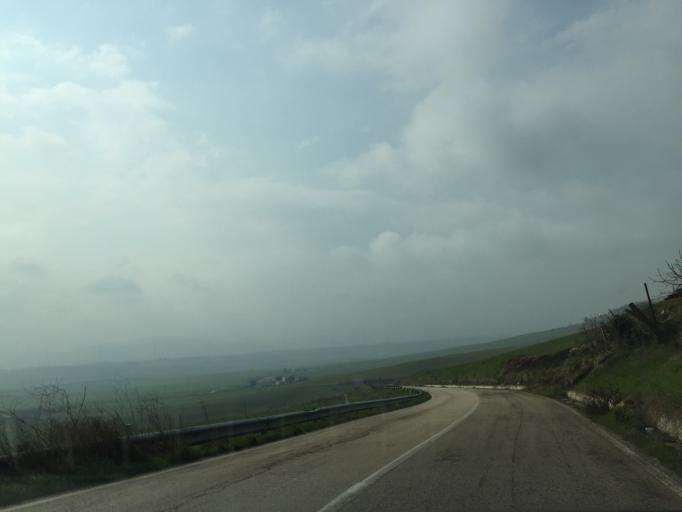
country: IT
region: Apulia
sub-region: Provincia di Foggia
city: Troia
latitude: 41.3665
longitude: 15.3275
